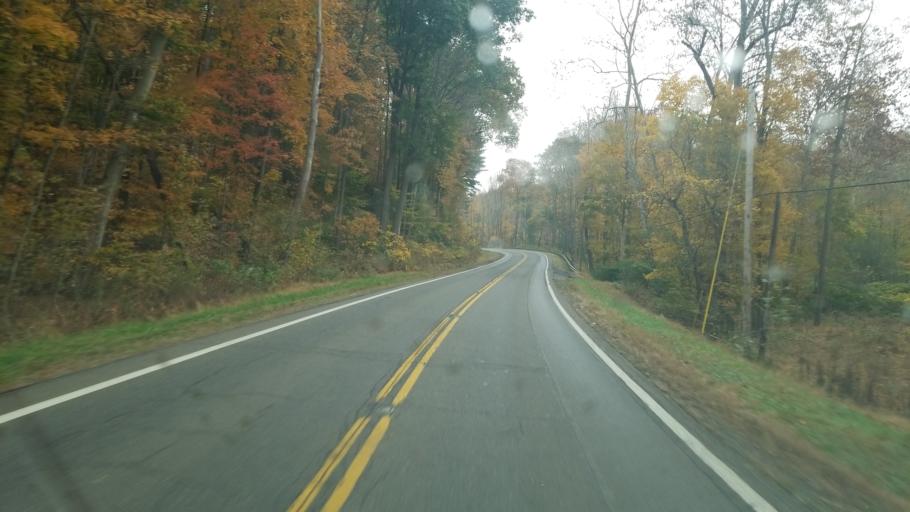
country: US
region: Ohio
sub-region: Holmes County
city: Millersburg
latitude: 40.5073
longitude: -81.9048
